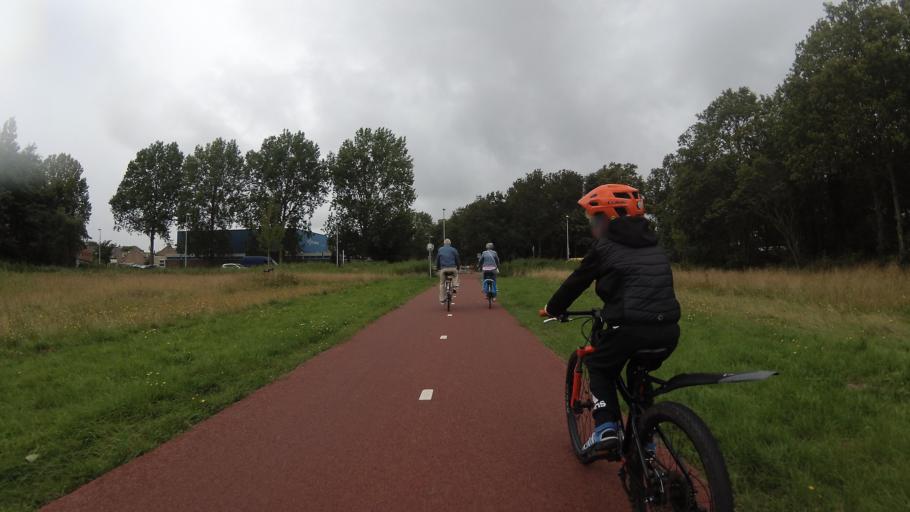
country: NL
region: North Holland
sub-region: Gemeente Den Helder
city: Den Helder
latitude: 52.9468
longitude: 4.7520
